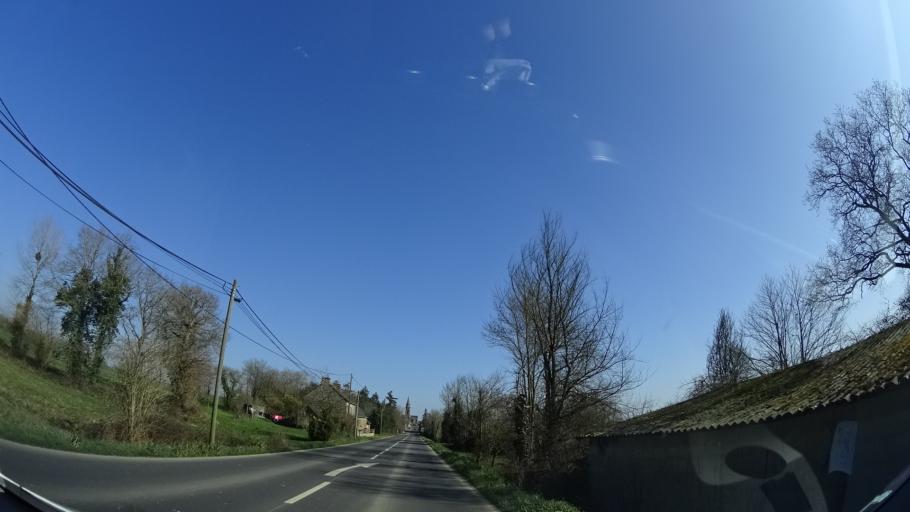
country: FR
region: Brittany
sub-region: Departement d'Ille-et-Vilaine
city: Meillac
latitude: 48.4125
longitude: -1.8208
